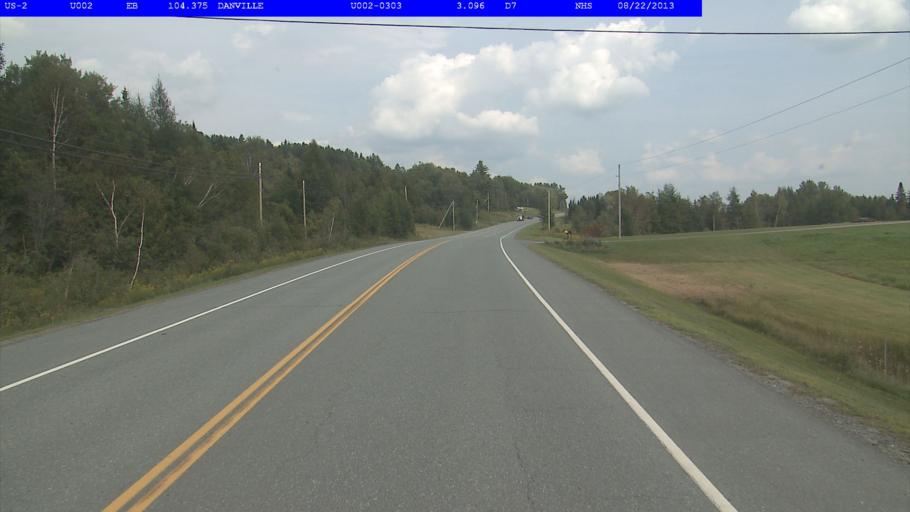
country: US
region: Vermont
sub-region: Caledonia County
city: Saint Johnsbury
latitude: 44.4110
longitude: -72.1671
